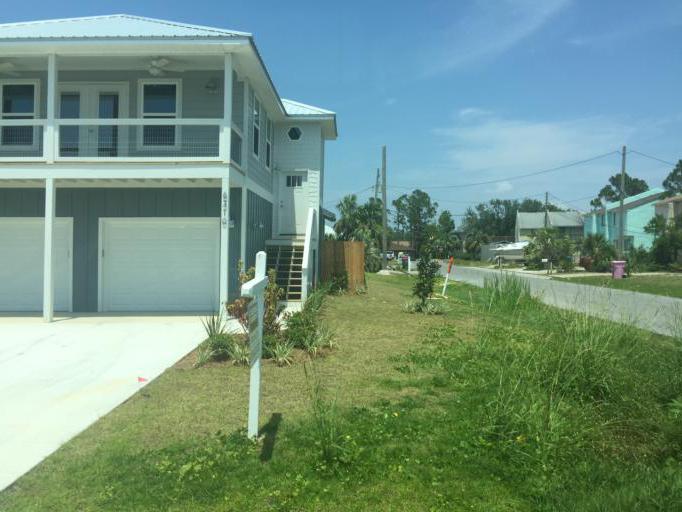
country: US
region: Florida
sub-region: Bay County
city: Lower Grand Lagoon
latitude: 30.1536
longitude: -85.7628
